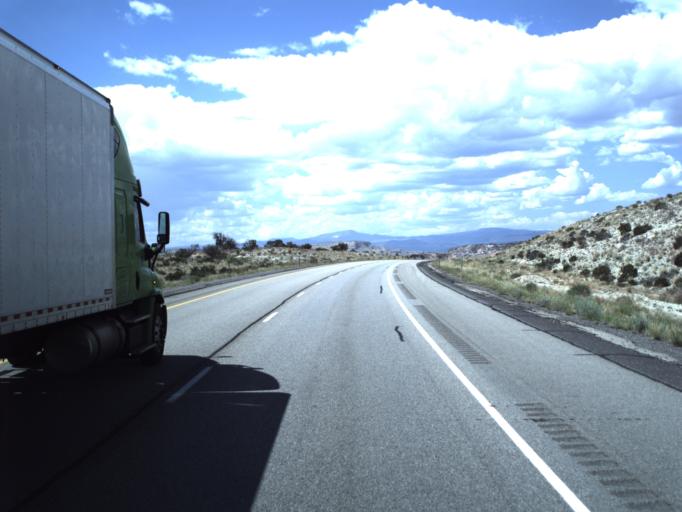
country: US
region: Utah
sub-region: Emery County
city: Ferron
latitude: 38.8318
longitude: -111.1113
